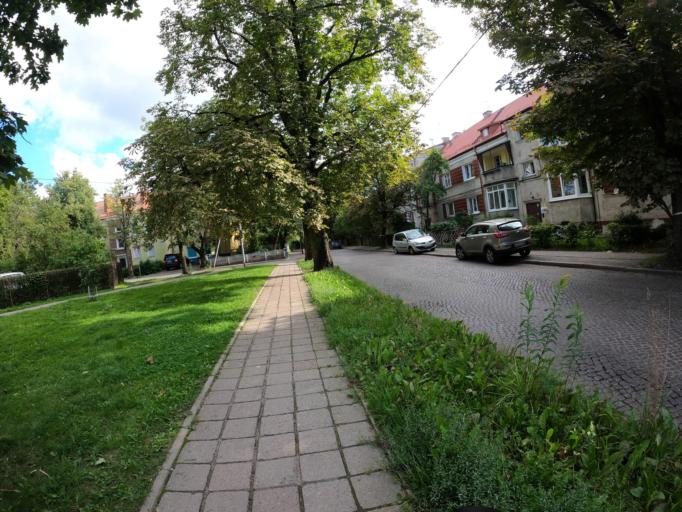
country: RU
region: Kaliningrad
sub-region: Gorod Kaliningrad
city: Kaliningrad
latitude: 54.7277
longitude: 20.4686
